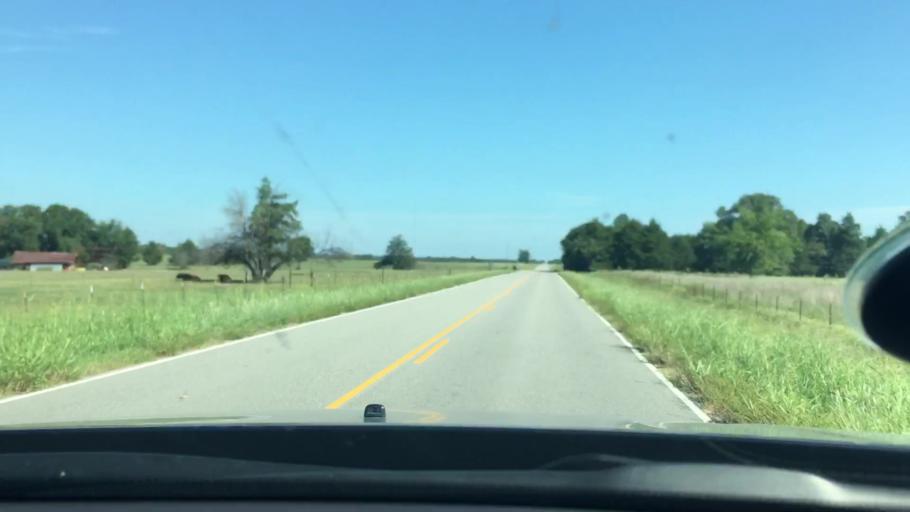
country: US
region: Oklahoma
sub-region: Johnston County
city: Tishomingo
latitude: 34.2999
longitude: -96.5488
